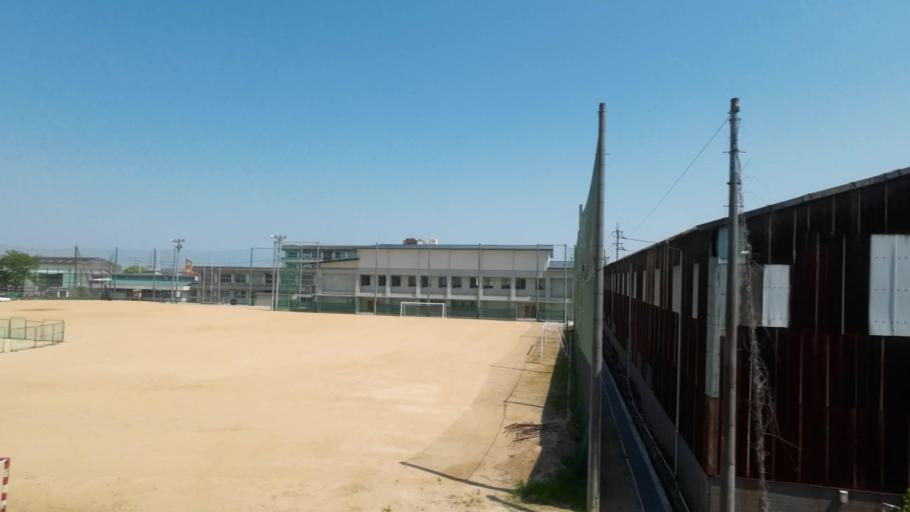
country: JP
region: Ehime
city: Saijo
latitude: 33.8964
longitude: 133.1372
